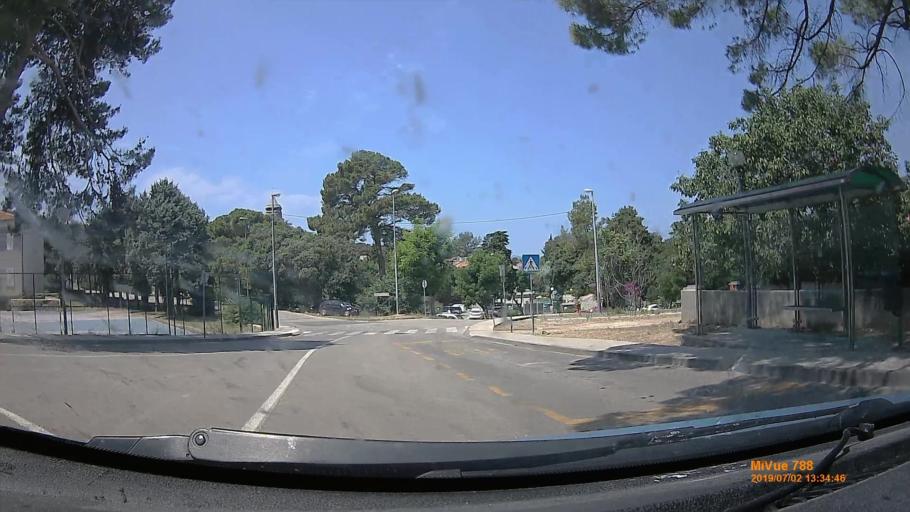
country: HR
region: Primorsko-Goranska
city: Mali Losinj
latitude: 44.5178
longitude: 14.5039
